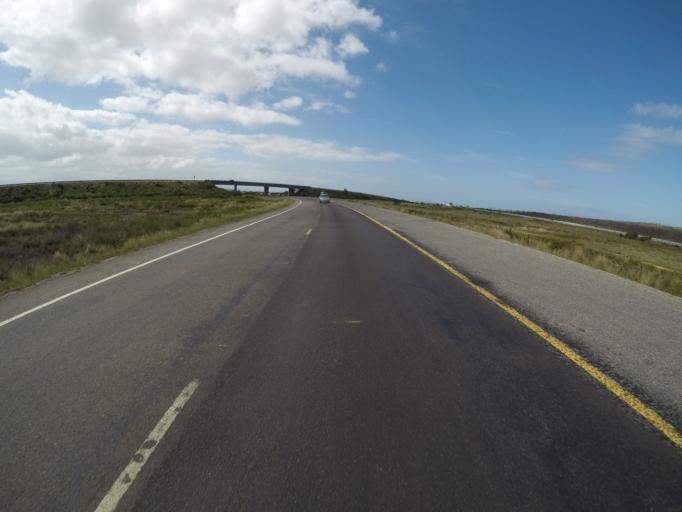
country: ZA
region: Western Cape
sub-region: Eden District Municipality
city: Mossel Bay
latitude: -34.1831
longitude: 22.0583
